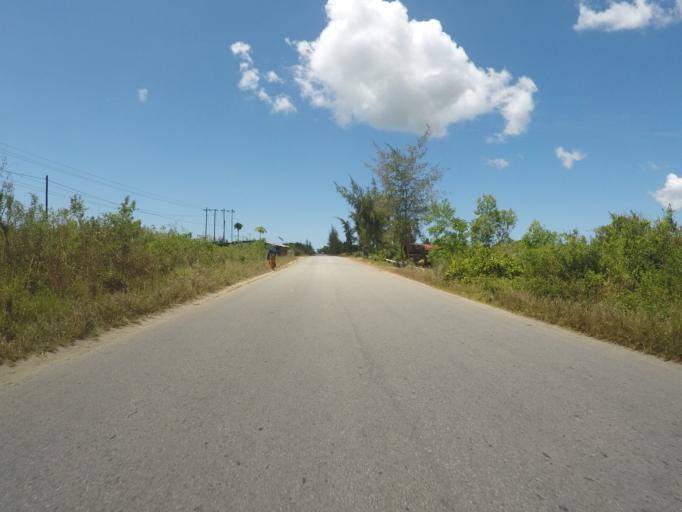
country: TZ
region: Zanzibar Central/South
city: Nganane
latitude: -6.2829
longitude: 39.4676
